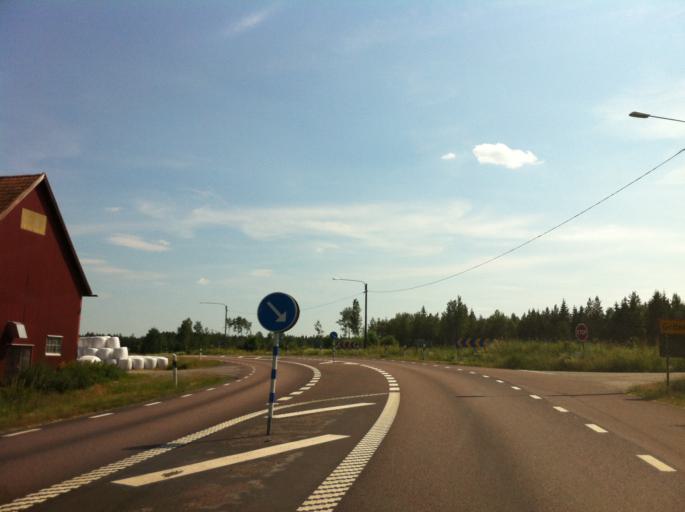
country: SE
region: Kalmar
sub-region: Nybro Kommun
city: Nybro
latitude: 56.7978
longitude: 15.7871
